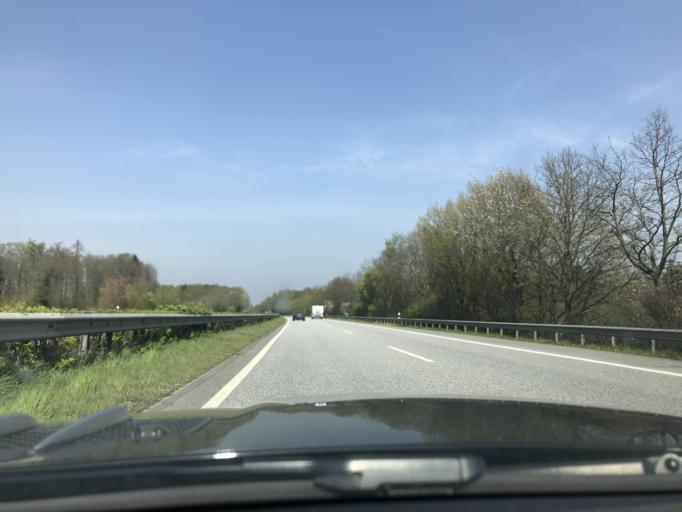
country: DE
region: Schleswig-Holstein
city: Beschendorf
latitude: 54.1844
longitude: 10.8939
